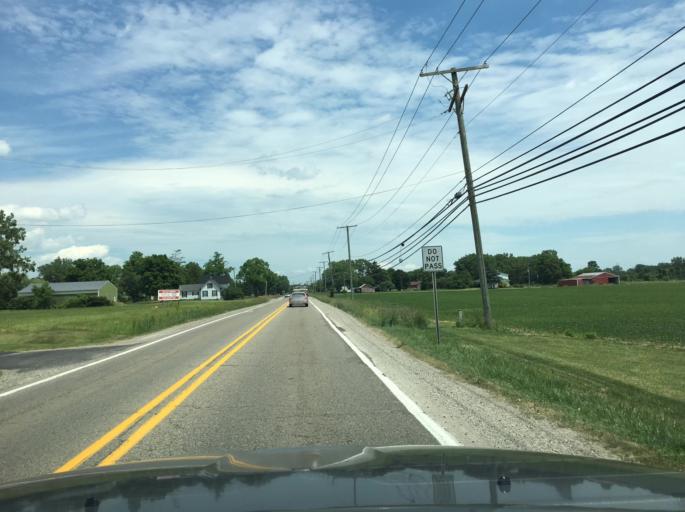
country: US
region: Michigan
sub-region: Macomb County
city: Shelby
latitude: 42.7148
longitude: -82.9943
